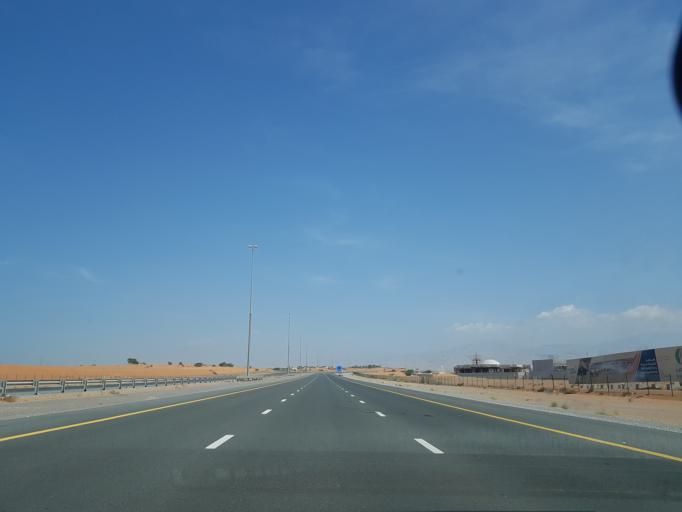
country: AE
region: Ra's al Khaymah
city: Ras al-Khaimah
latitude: 25.7001
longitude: 55.9320
